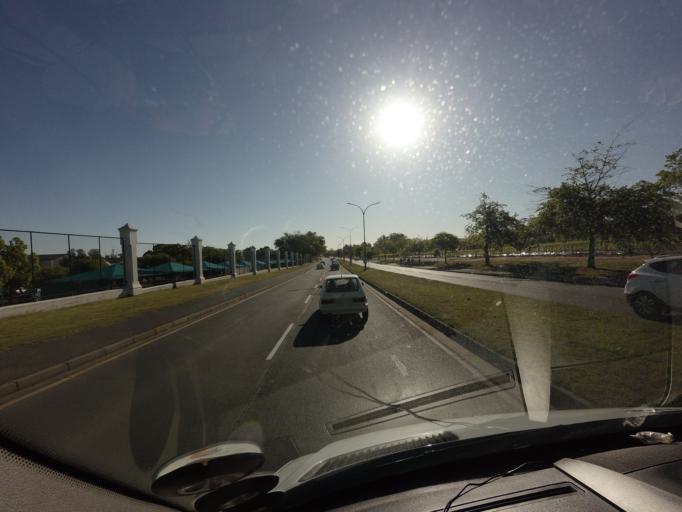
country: ZA
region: Western Cape
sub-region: Cape Winelands District Municipality
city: Stellenbosch
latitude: -33.9423
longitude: 18.8417
